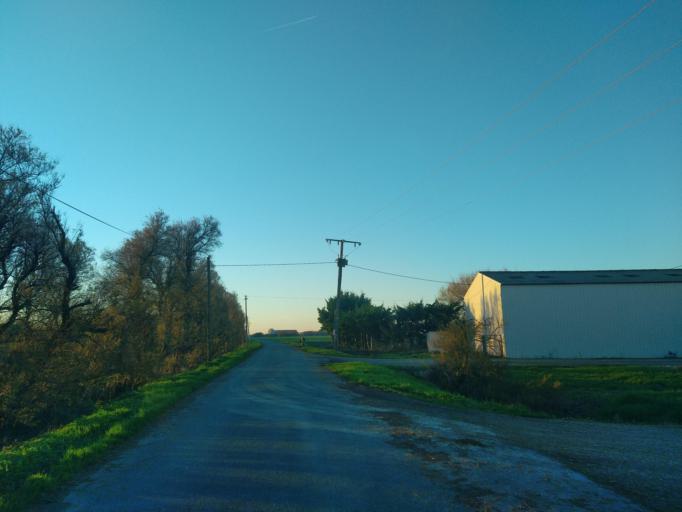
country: FR
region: Pays de la Loire
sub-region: Departement de la Vendee
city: Triaize
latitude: 46.3731
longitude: -1.2844
